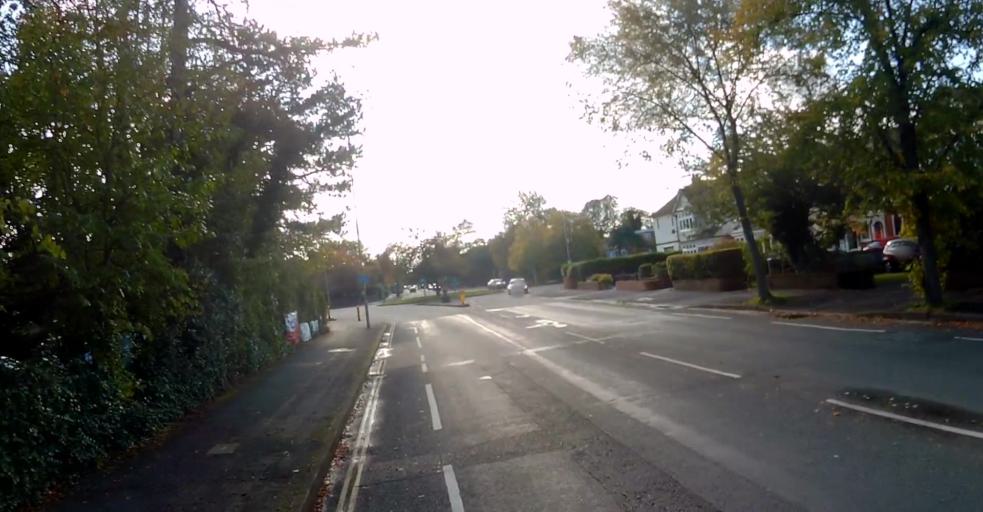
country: GB
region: England
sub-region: Hampshire
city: Farnborough
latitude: 51.2807
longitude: -0.7504
